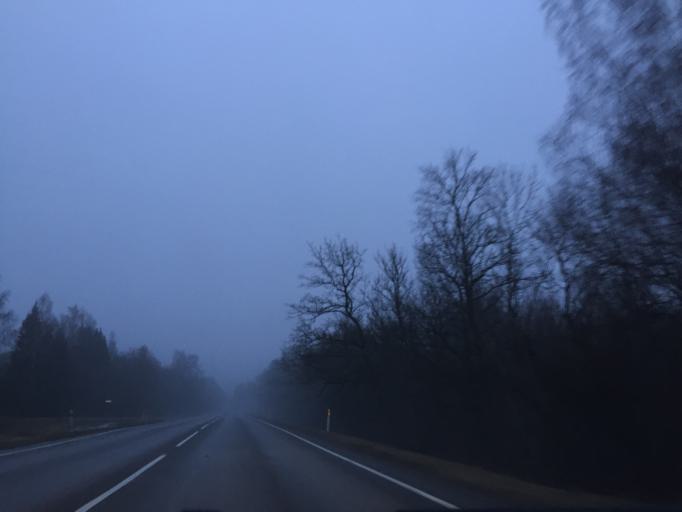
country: EE
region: Laeaene
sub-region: Lihula vald
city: Lihula
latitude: 58.6350
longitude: 23.6884
